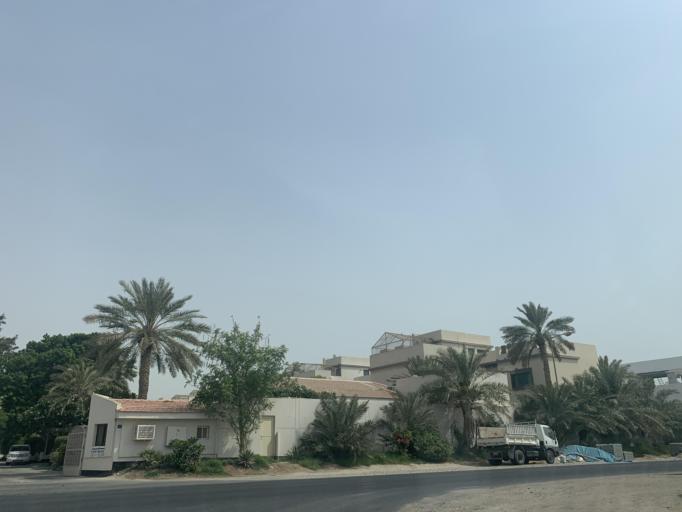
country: BH
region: Manama
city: Jidd Hafs
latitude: 26.2012
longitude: 50.4726
